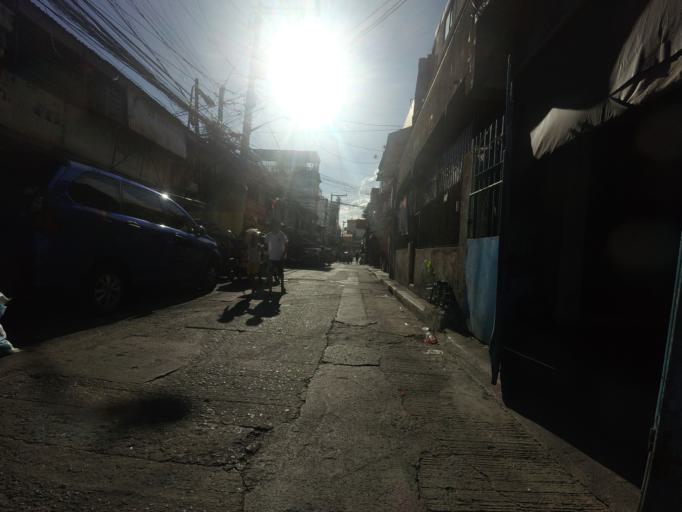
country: PH
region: Metro Manila
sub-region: Mandaluyong
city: Mandaluyong City
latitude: 14.5873
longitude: 121.0282
